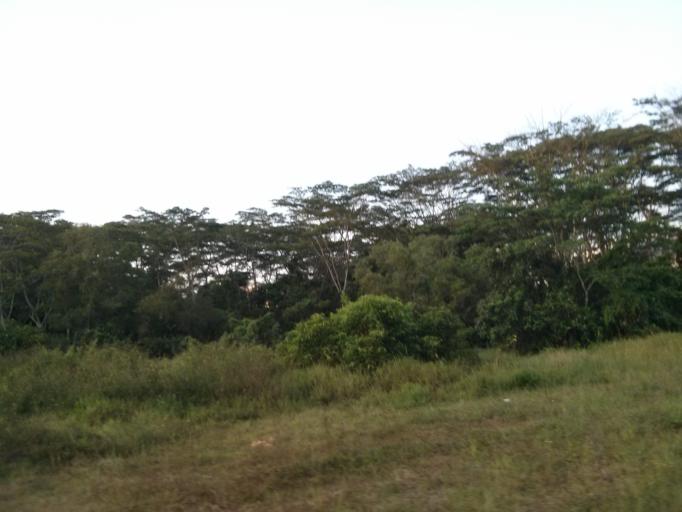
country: MY
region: Johor
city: Johor Bahru
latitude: 1.3732
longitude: 103.7344
